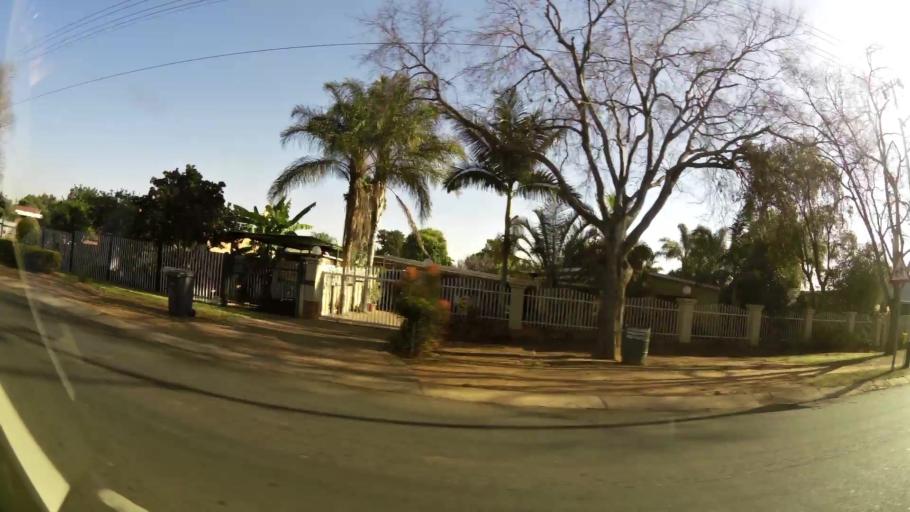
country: ZA
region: Gauteng
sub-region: City of Tshwane Metropolitan Municipality
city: Pretoria
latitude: -25.7101
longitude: 28.2557
